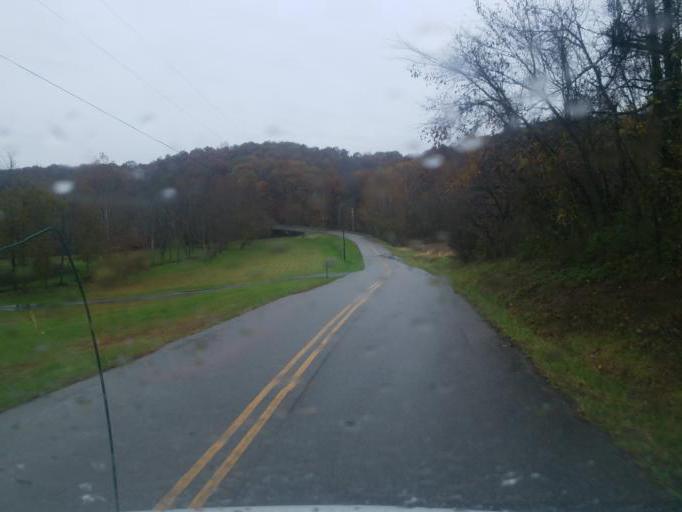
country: US
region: West Virginia
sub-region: Wood County
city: Vienna
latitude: 39.4216
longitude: -81.6118
